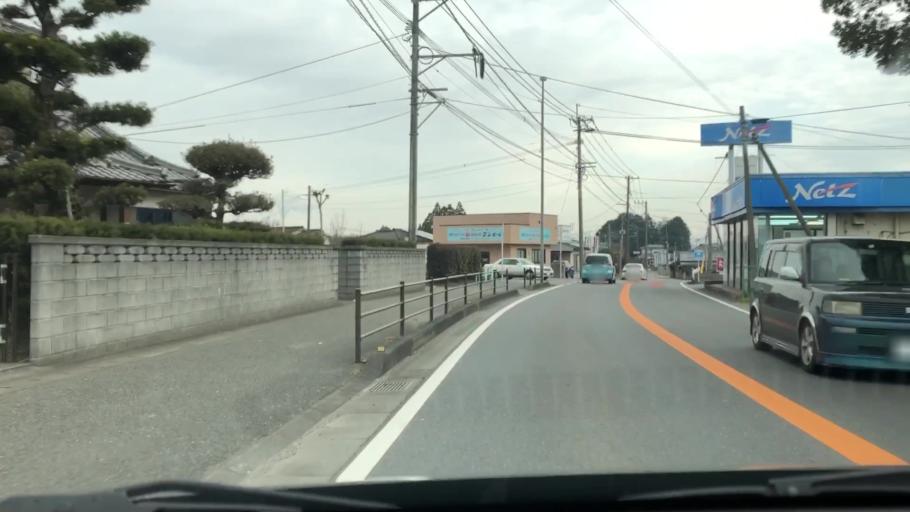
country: JP
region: Oita
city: Takedamachi
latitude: 32.9909
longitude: 131.6101
